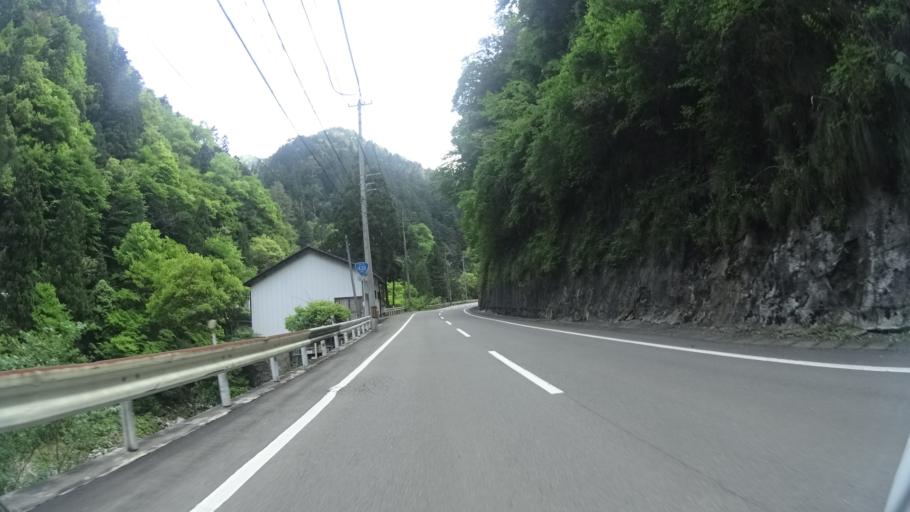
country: JP
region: Tokushima
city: Wakimachi
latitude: 33.9391
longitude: 134.0622
